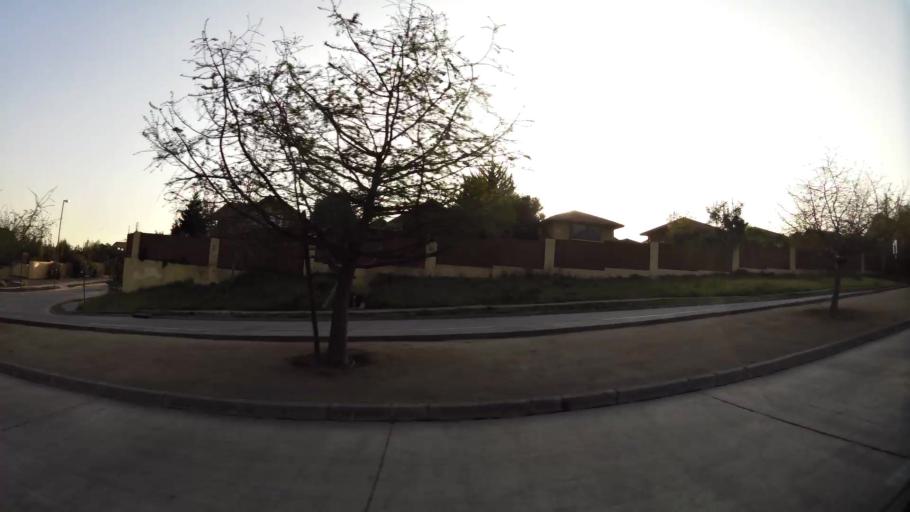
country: CL
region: Santiago Metropolitan
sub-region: Provincia de Santiago
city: Villa Presidente Frei, Nunoa, Santiago, Chile
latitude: -33.3315
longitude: -70.5113
